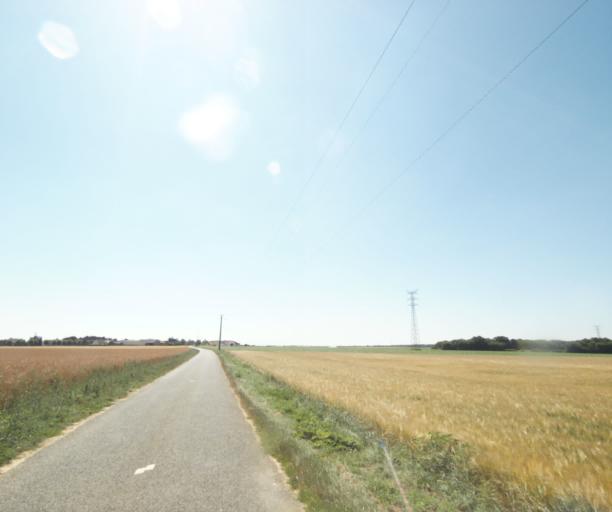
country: FR
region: Ile-de-France
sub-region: Departement de Seine-et-Marne
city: Noisy-sur-Ecole
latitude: 48.3089
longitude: 2.4817
